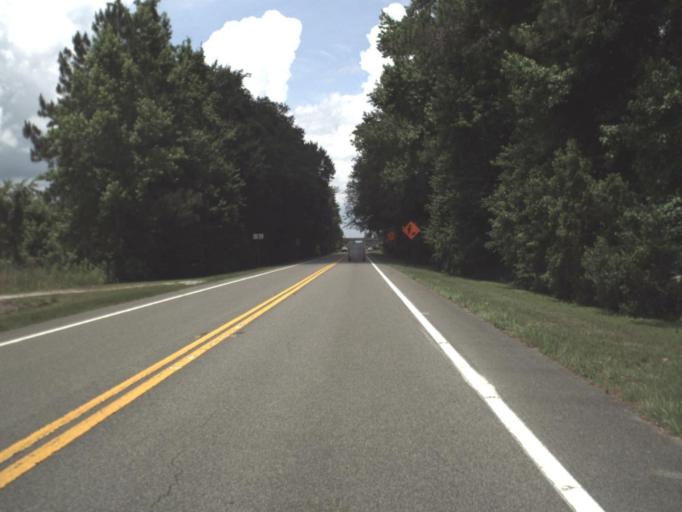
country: US
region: Florida
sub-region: Nassau County
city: Yulee
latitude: 30.7043
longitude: -81.6663
